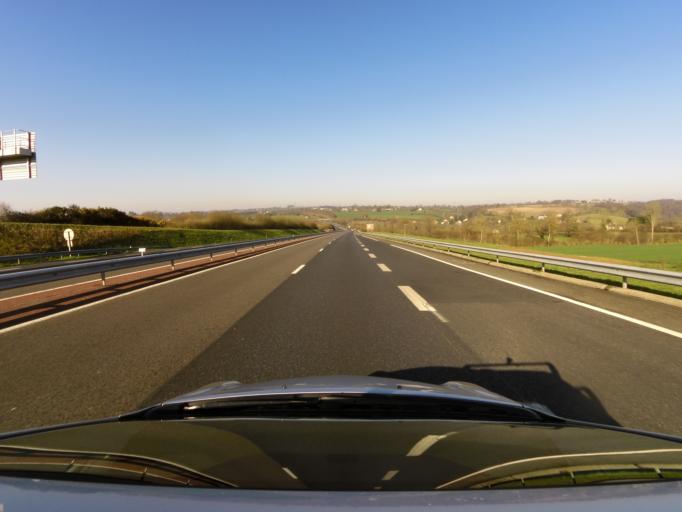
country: FR
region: Lower Normandy
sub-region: Departement de la Manche
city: Villedieu-les-Poeles
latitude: 48.8585
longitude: -1.2096
